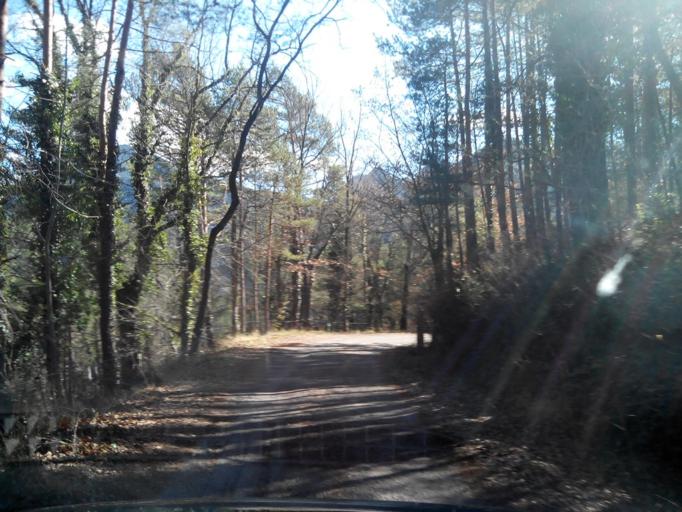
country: ES
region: Catalonia
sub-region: Provincia de Barcelona
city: Vilada
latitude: 42.1320
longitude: 1.9279
